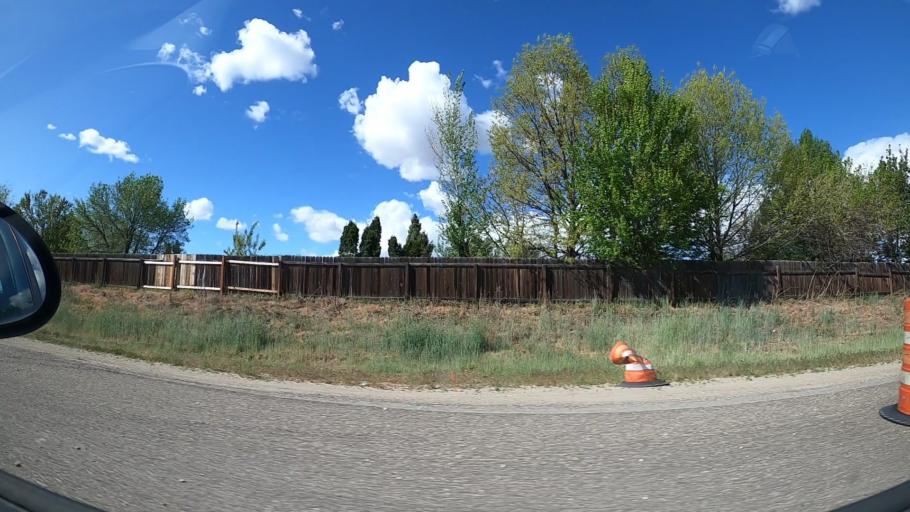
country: US
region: Idaho
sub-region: Ada County
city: Eagle
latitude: 43.6921
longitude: -116.3600
